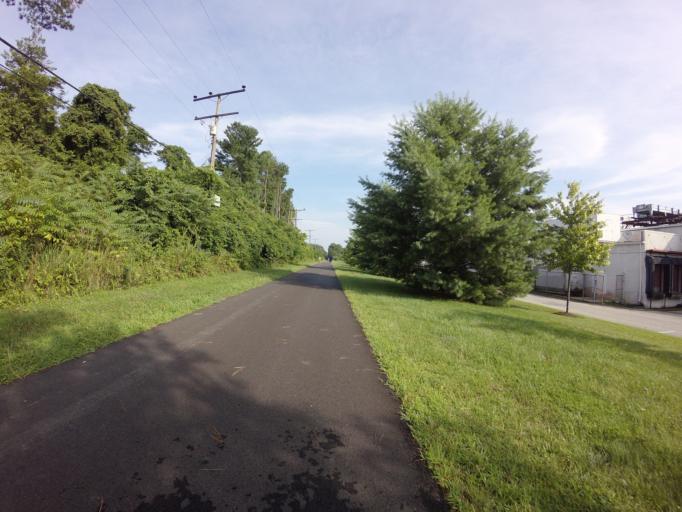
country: US
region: Maryland
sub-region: Anne Arundel County
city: Pasadena
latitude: 39.1243
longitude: -76.5923
